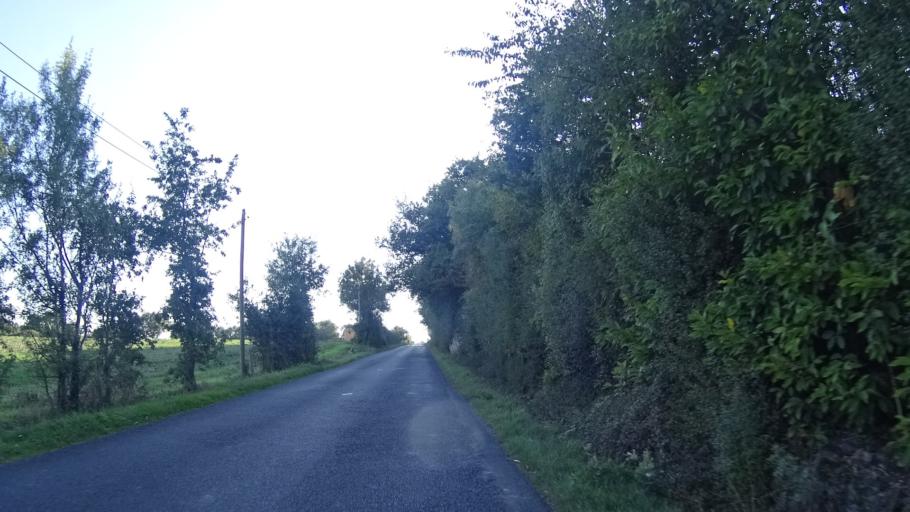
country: FR
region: Pays de la Loire
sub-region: Departement de Maine-et-Loire
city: Bouzille
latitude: 47.3434
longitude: -1.0870
